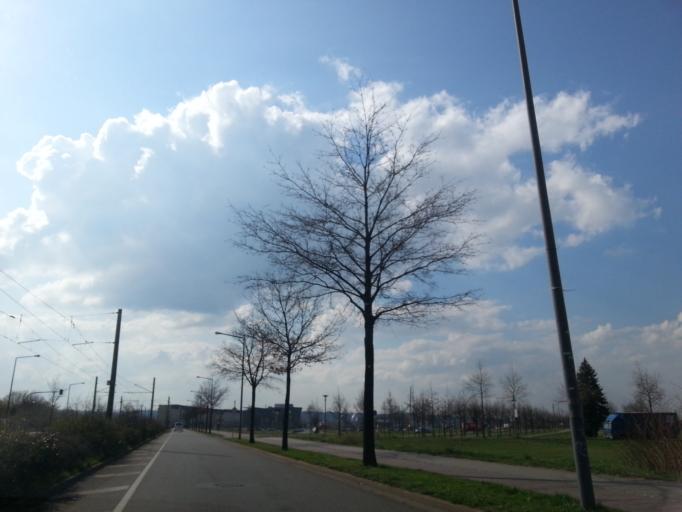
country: DE
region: Saxony
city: Dresden
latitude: 51.0785
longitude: 13.7052
